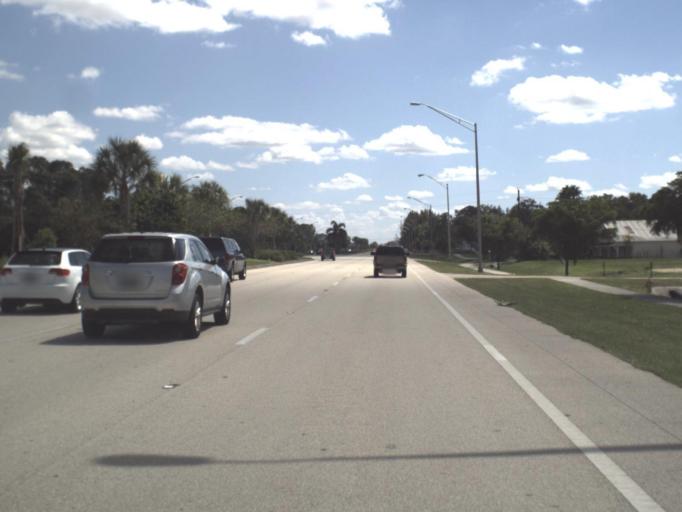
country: US
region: Florida
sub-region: Collier County
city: Naples Manor
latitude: 26.0903
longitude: -81.7328
